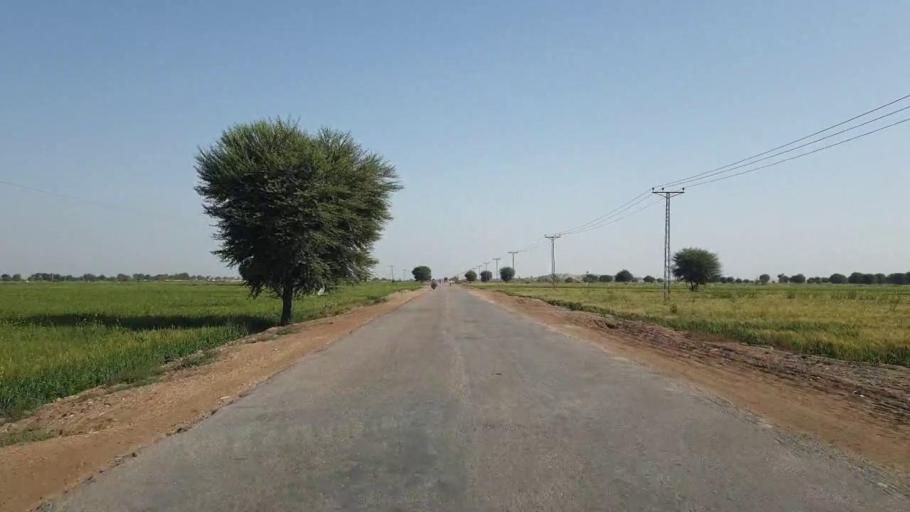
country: PK
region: Sindh
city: Umarkot
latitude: 25.4157
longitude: 69.7320
